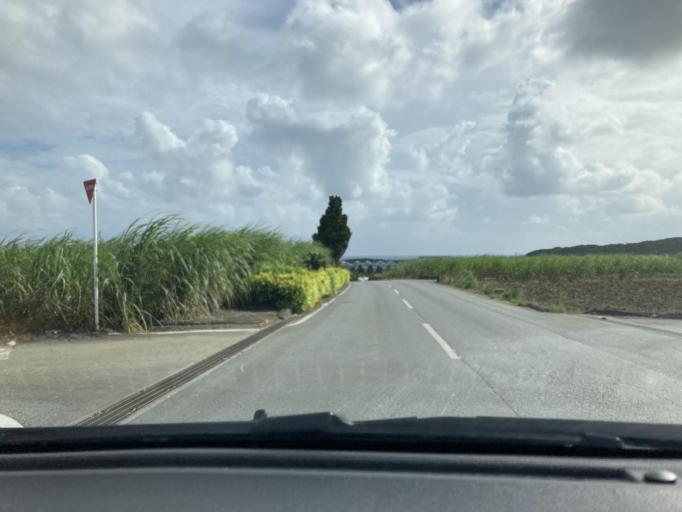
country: JP
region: Okinawa
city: Itoman
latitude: 26.0925
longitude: 127.6940
